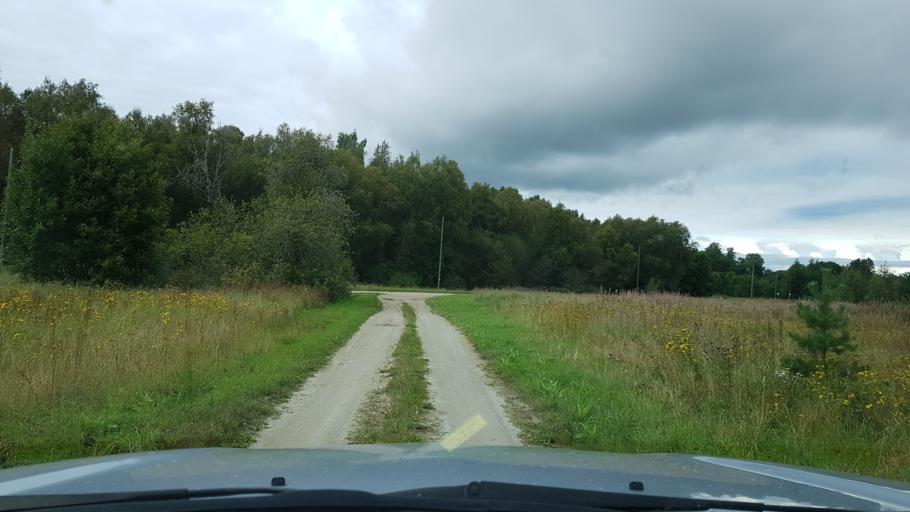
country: EE
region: Harju
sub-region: Raasiku vald
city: Arukula
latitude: 59.3597
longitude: 25.0055
